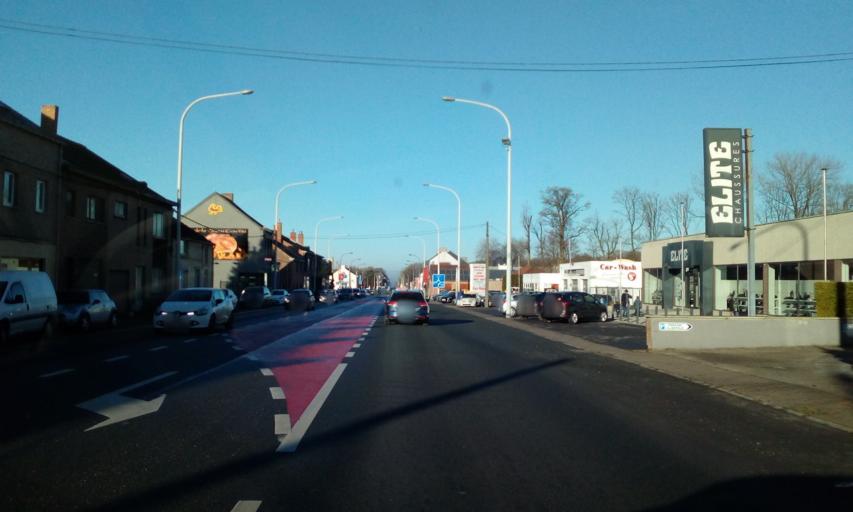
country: BE
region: Wallonia
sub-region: Province du Hainaut
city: Gerpinnes
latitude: 50.3405
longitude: 4.4739
